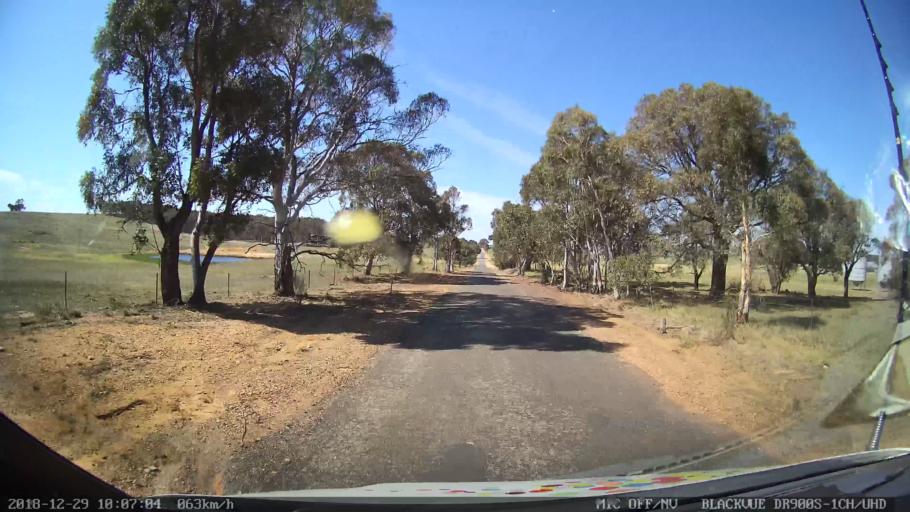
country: AU
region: New South Wales
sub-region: Yass Valley
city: Gundaroo
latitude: -34.8491
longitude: 149.4539
